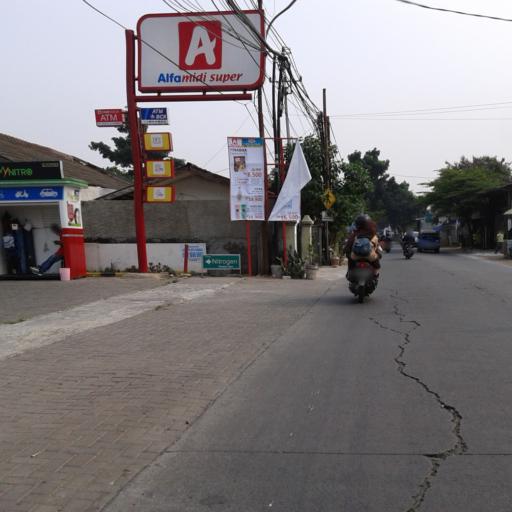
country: ID
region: West Java
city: Sawangan
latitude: -6.3674
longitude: 106.7747
